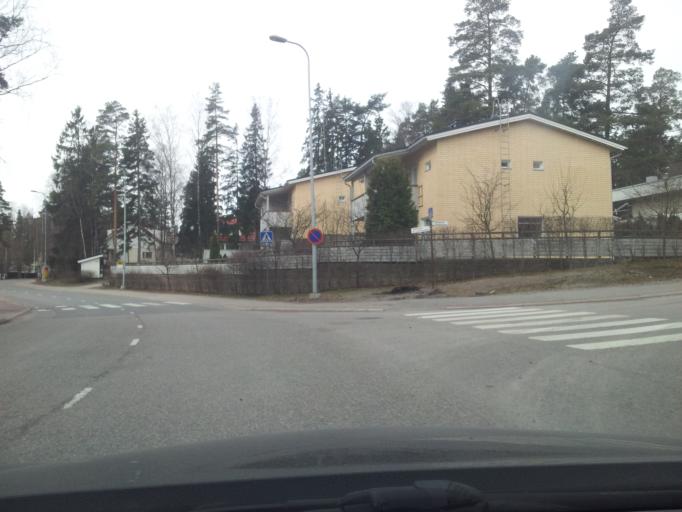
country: FI
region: Uusimaa
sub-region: Helsinki
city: Kilo
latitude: 60.2048
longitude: 24.8009
